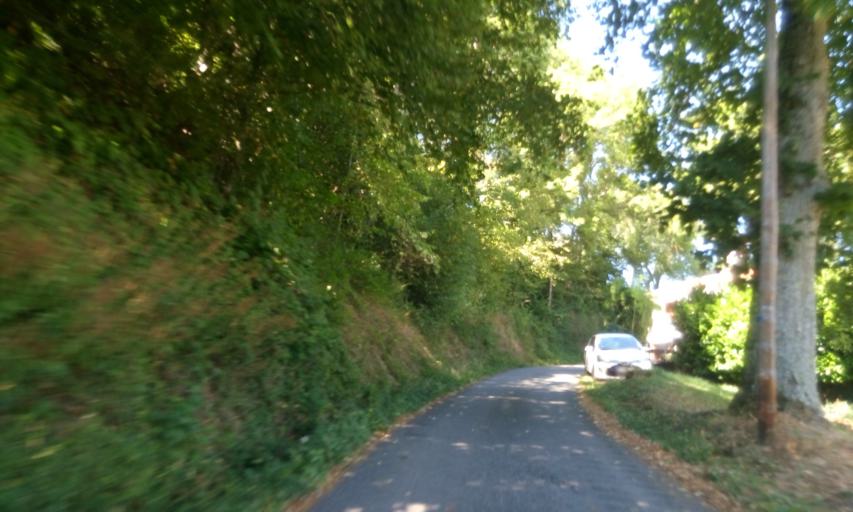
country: FR
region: Rhone-Alpes
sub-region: Departement du Rhone
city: Grandris
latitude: 45.9949
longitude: 4.4350
